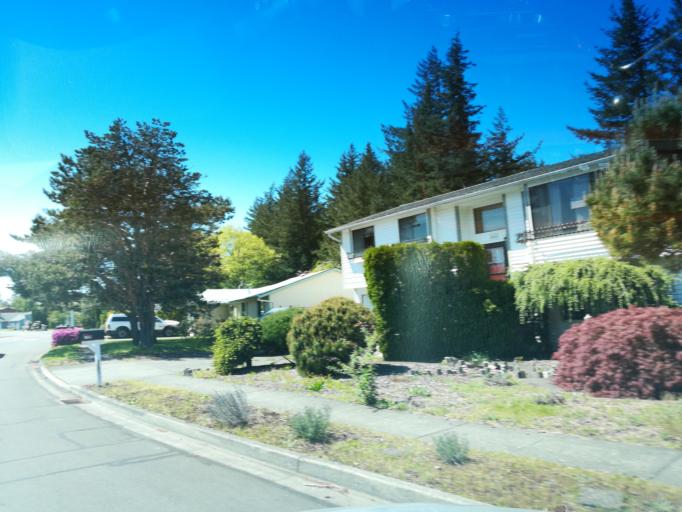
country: US
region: Oregon
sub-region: Multnomah County
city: Troutdale
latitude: 45.5273
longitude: -122.3777
